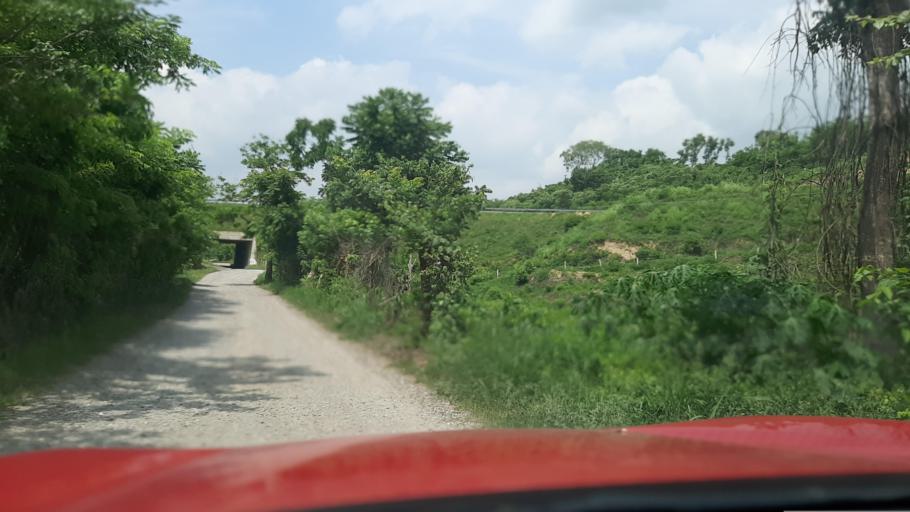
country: MX
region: Veracruz
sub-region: Papantla
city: Polutla
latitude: 20.4525
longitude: -97.2413
